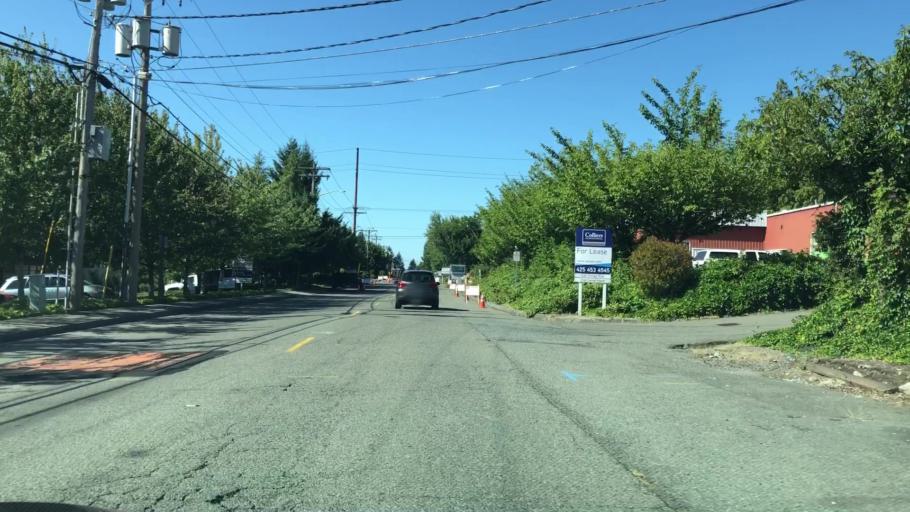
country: US
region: Washington
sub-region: King County
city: Woodinville
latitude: 47.7677
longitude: -122.1477
